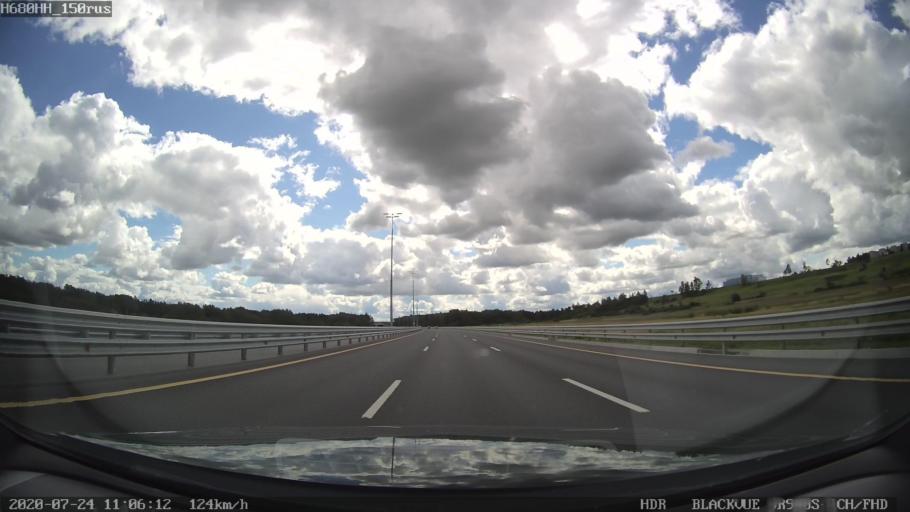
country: RU
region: St.-Petersburg
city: Shushary
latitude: 59.7665
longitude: 30.3692
